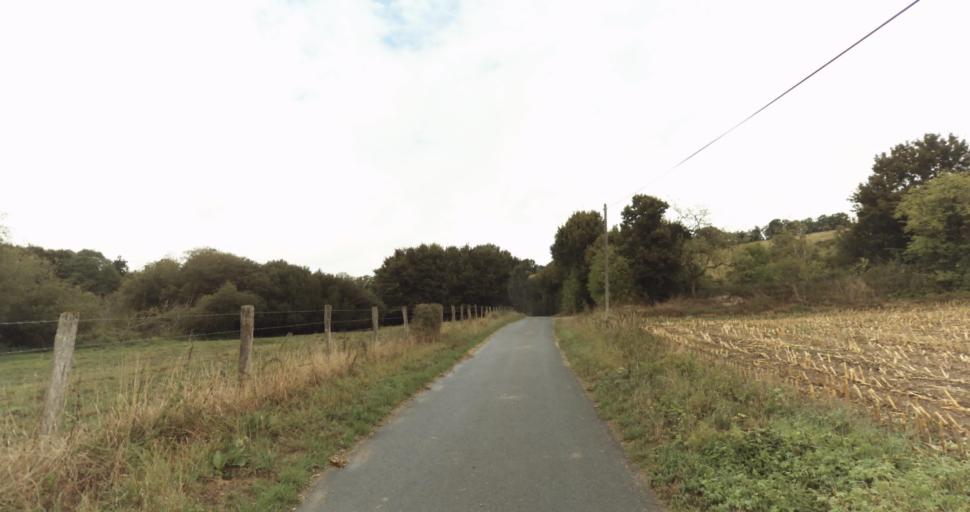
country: FR
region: Lower Normandy
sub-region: Departement de l'Orne
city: Vimoutiers
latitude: 48.8561
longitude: 0.2374
